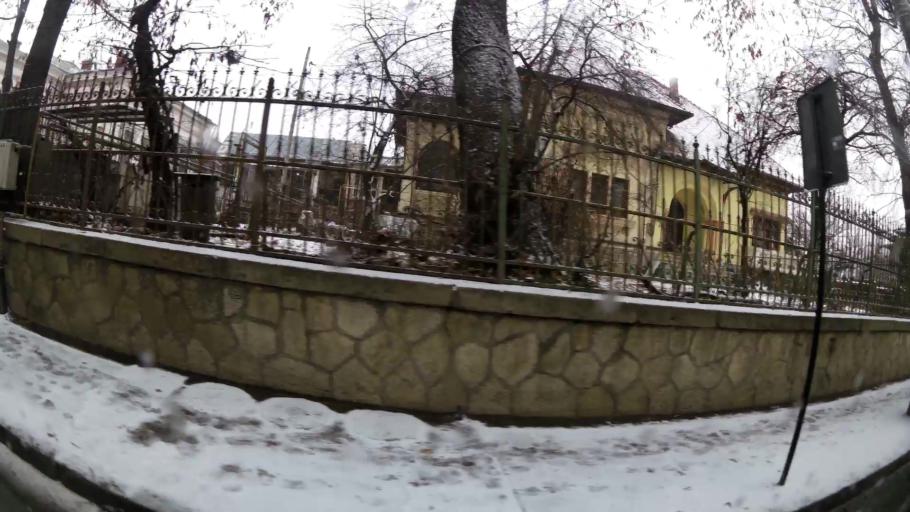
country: RO
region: Dambovita
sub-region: Municipiul Targoviste
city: Targoviste
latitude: 44.9300
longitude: 25.4611
